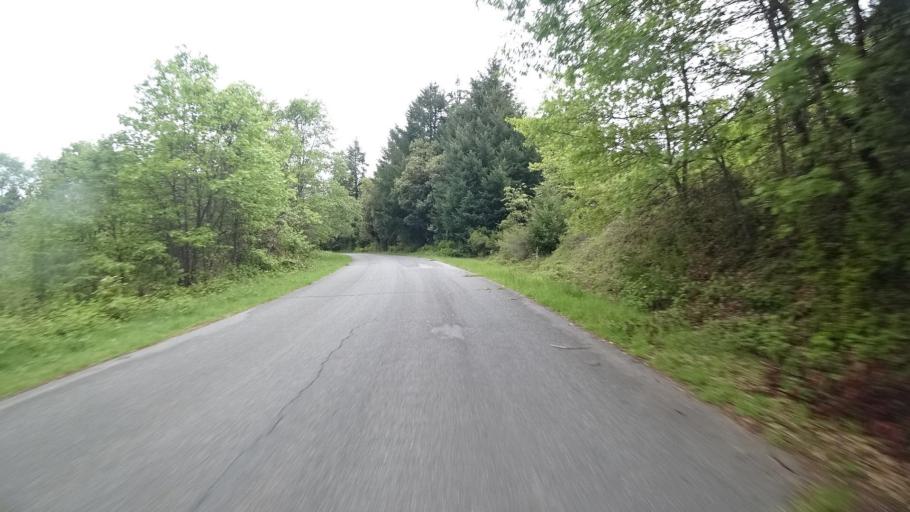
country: US
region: California
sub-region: Humboldt County
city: Willow Creek
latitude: 41.1163
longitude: -123.7197
